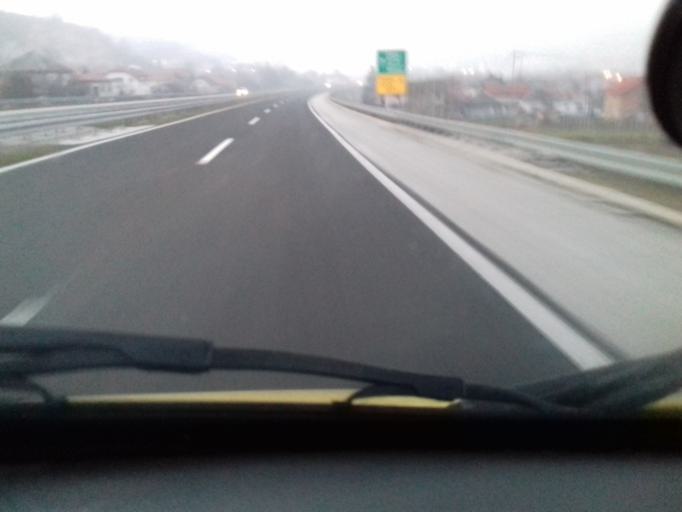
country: BA
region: Federation of Bosnia and Herzegovina
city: Kakanj
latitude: 44.1180
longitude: 18.1066
